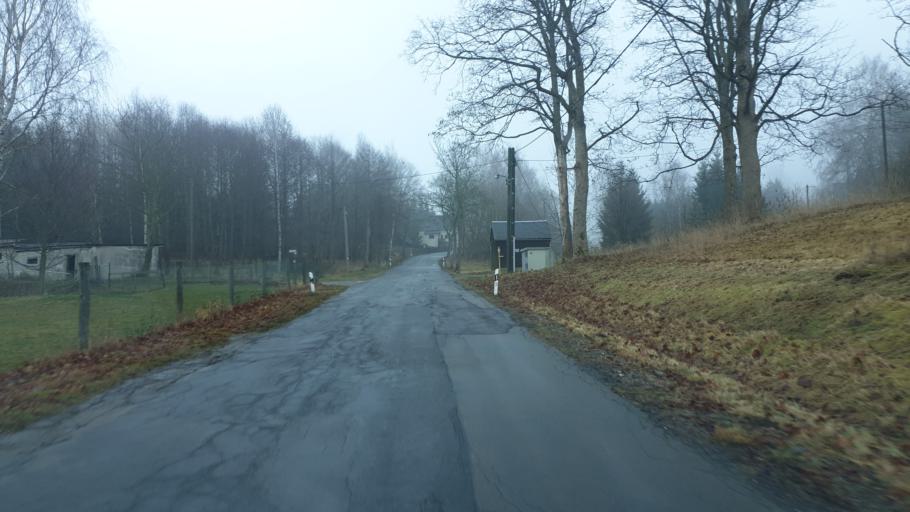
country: DE
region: Saxony
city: Pfaffroda
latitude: 50.7379
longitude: 13.3649
